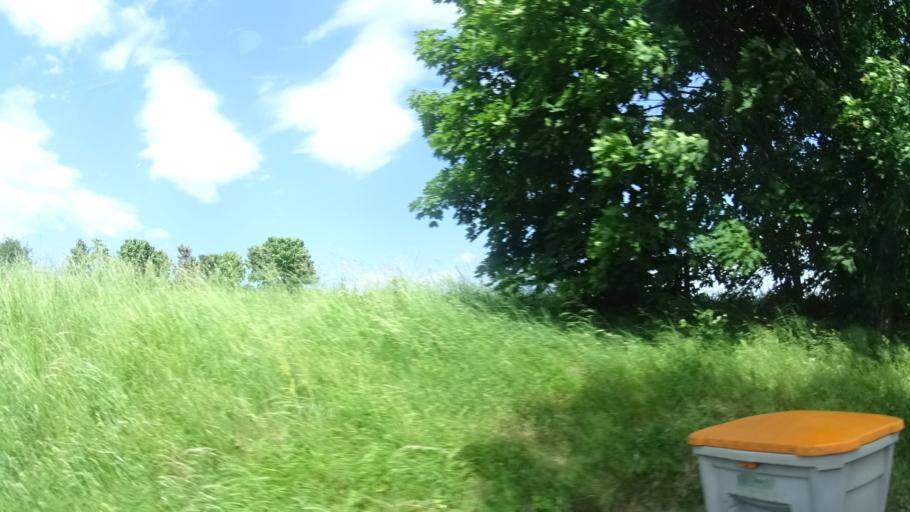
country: DE
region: Hesse
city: Haina
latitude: 51.0571
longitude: 8.9844
